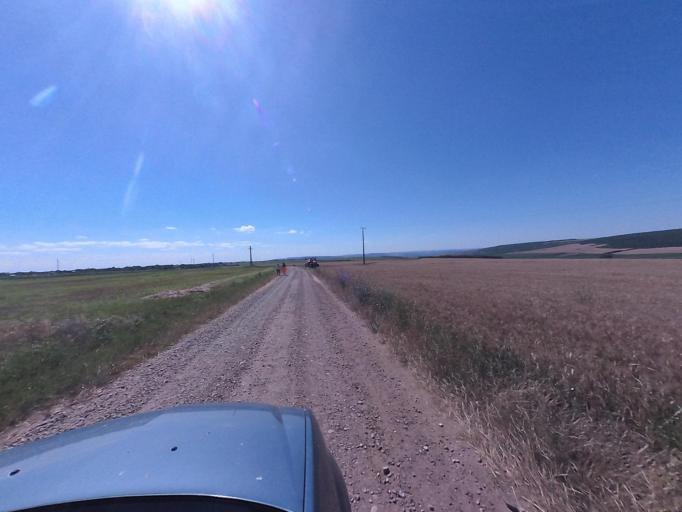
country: RO
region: Vaslui
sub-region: Comuna Costesti
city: Costesti
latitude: 46.4808
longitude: 27.7764
